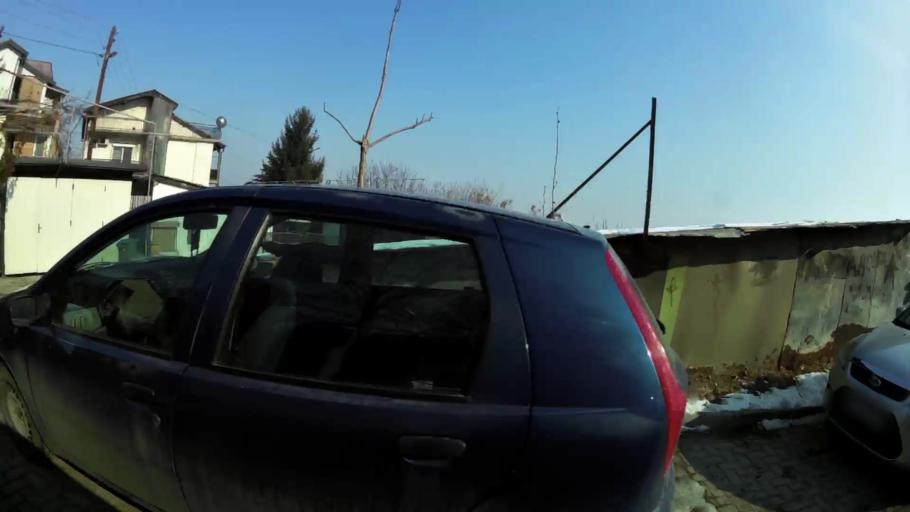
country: MK
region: Sopiste
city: Sopishte
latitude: 41.9739
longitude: 21.4365
